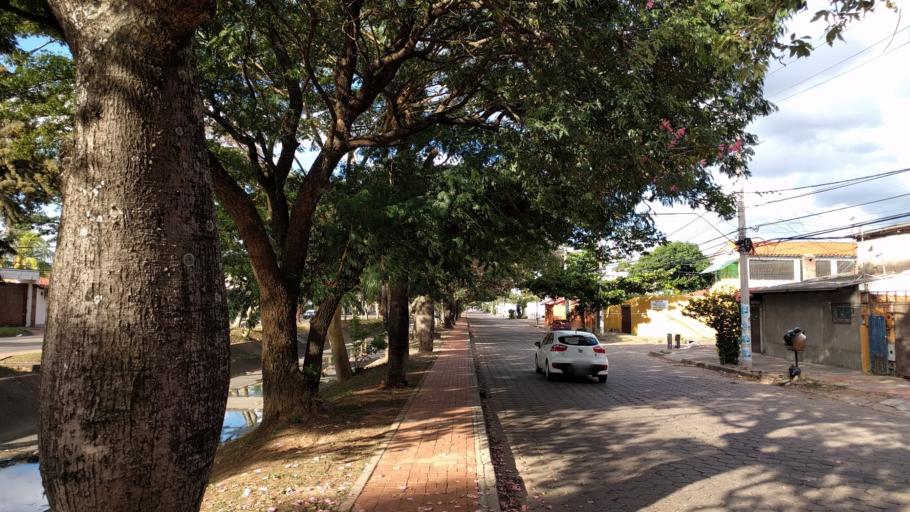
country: BO
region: Santa Cruz
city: Santa Cruz de la Sierra
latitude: -17.7772
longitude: -63.1587
